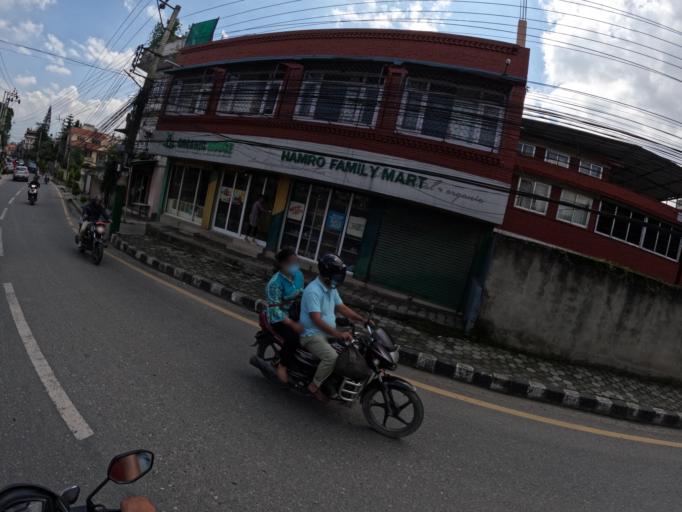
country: NP
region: Central Region
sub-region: Bagmati Zone
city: Patan
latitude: 27.6813
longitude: 85.3057
